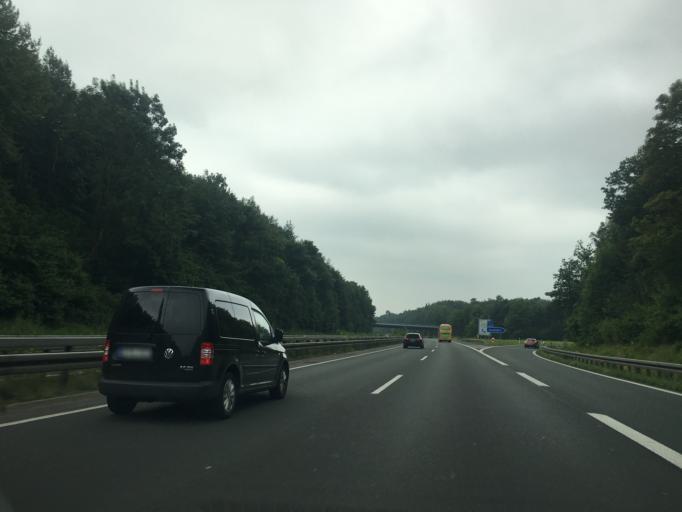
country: DE
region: North Rhine-Westphalia
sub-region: Regierungsbezirk Munster
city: Haltern
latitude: 51.7374
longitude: 7.1511
